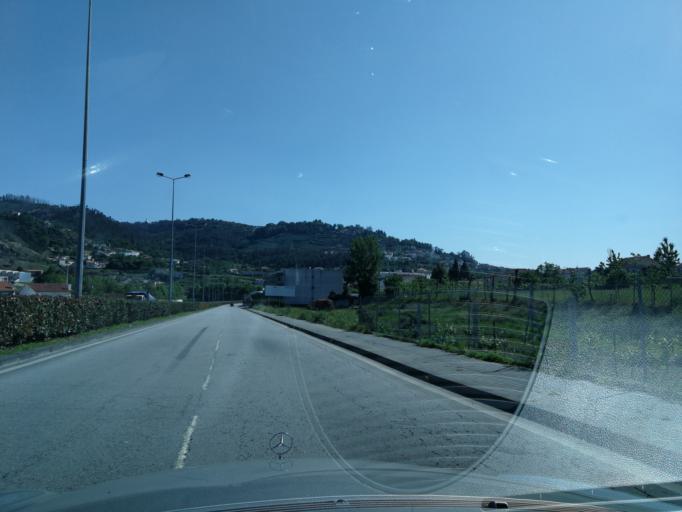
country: PT
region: Braga
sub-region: Braga
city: Adaufe
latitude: 41.5718
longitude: -8.3688
